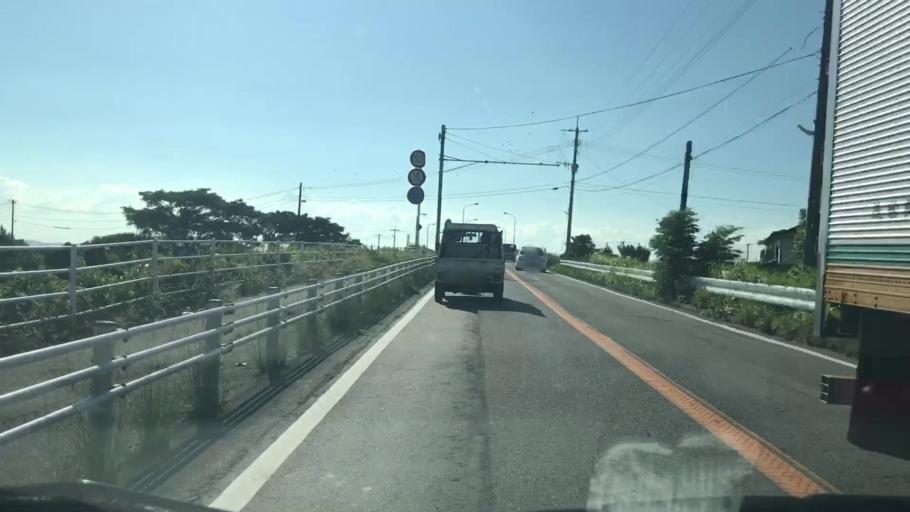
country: JP
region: Saga Prefecture
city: Saga-shi
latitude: 33.2189
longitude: 130.2617
